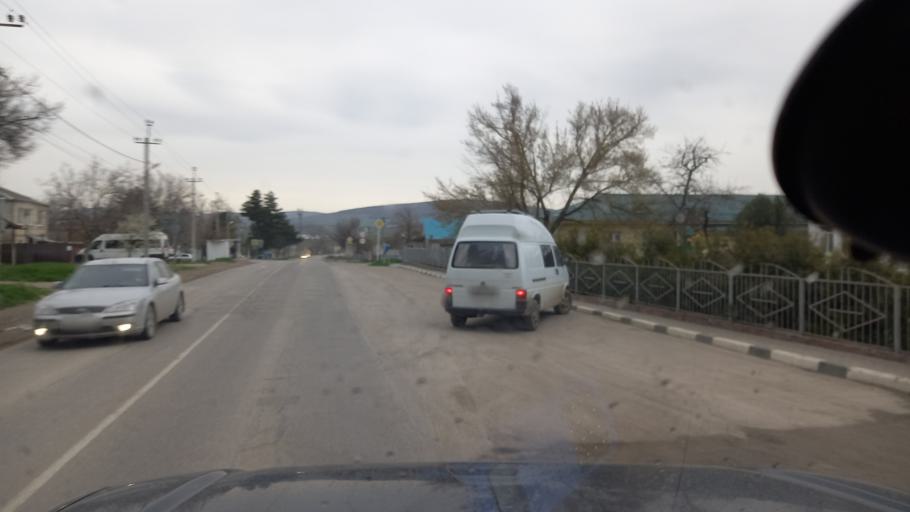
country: RU
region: Krasnodarskiy
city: Anapskaya
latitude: 44.8939
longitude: 37.4597
